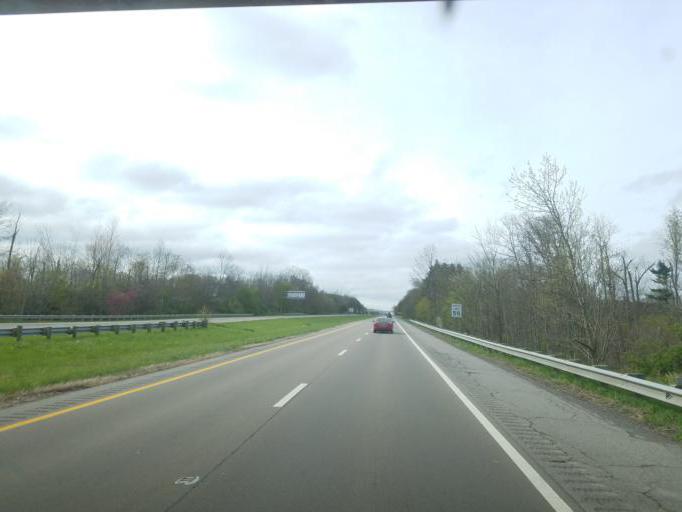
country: US
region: Ohio
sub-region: Wayne County
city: Wooster
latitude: 40.7847
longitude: -81.9145
